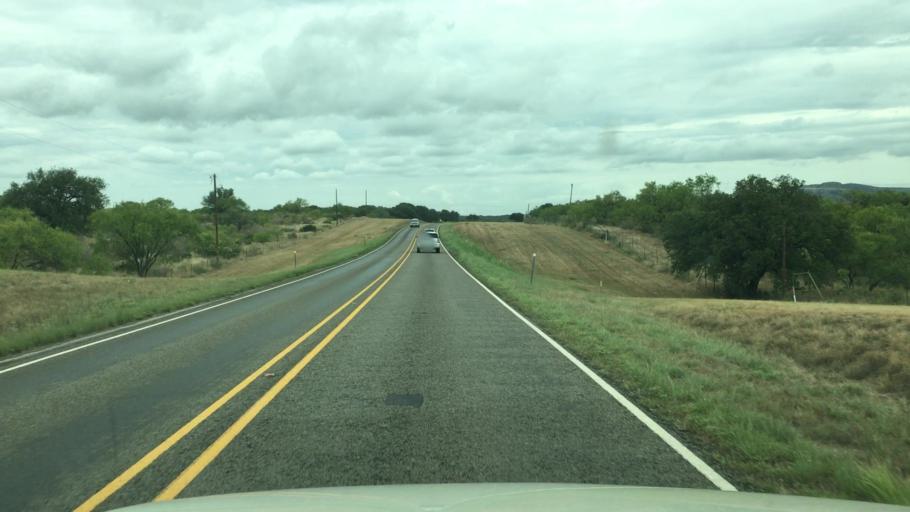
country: US
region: Texas
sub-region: Llano County
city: Kingsland
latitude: 30.5791
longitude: -98.4952
